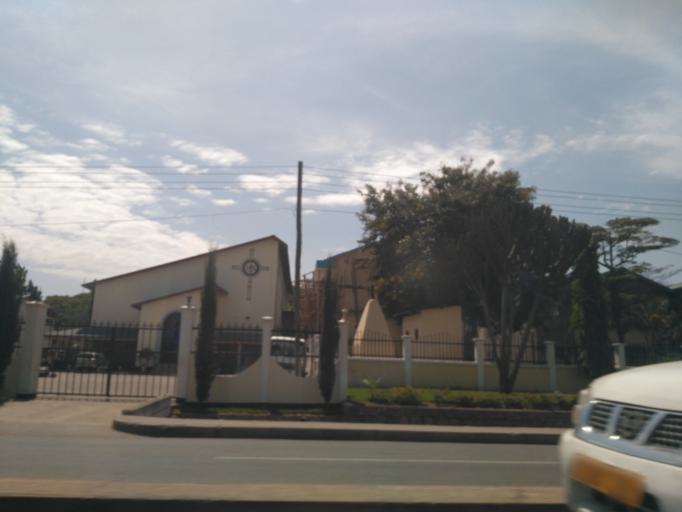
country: TZ
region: Mwanza
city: Mwanza
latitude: -2.5118
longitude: 32.8997
